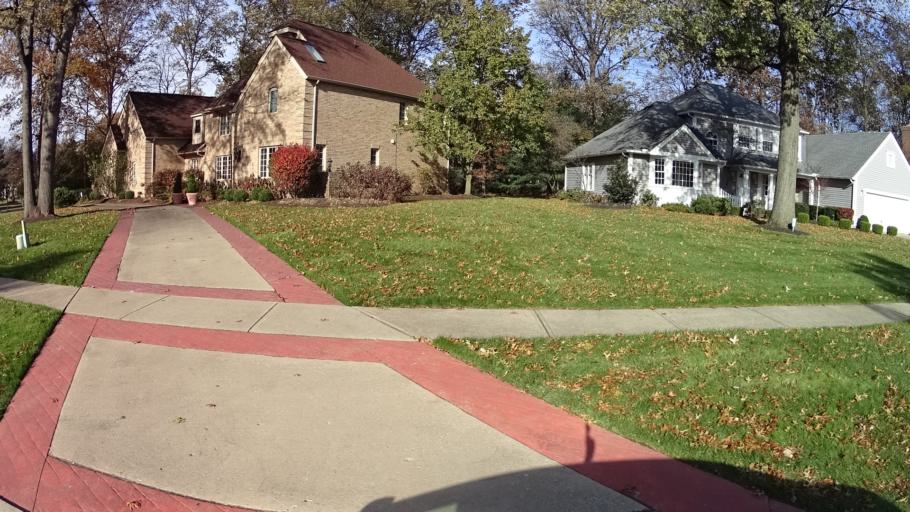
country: US
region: Ohio
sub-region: Lorain County
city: Avon Lake
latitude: 41.4976
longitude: -81.9773
